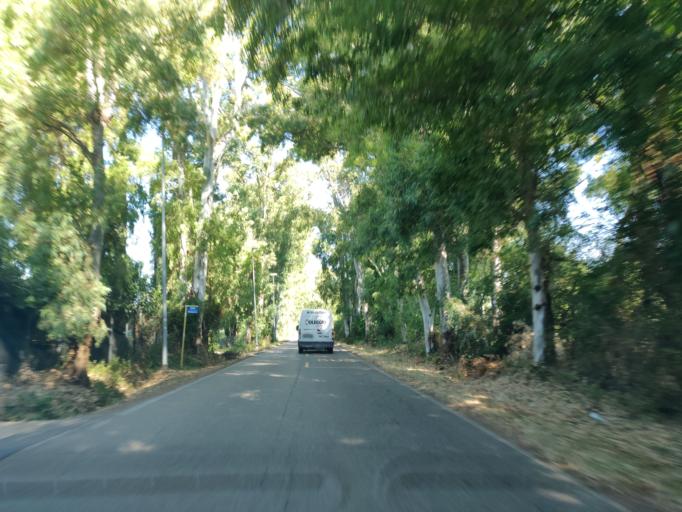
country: IT
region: Latium
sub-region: Citta metropolitana di Roma Capitale
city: Aurelia
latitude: 42.1581
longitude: 11.7513
